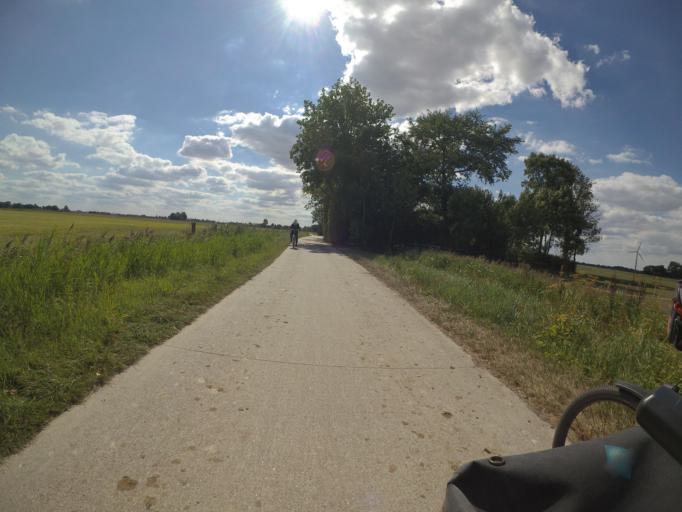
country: NL
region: Friesland
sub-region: Gemeente Kollumerland en Nieuwkruisland
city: Kollum
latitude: 53.2760
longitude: 6.2033
